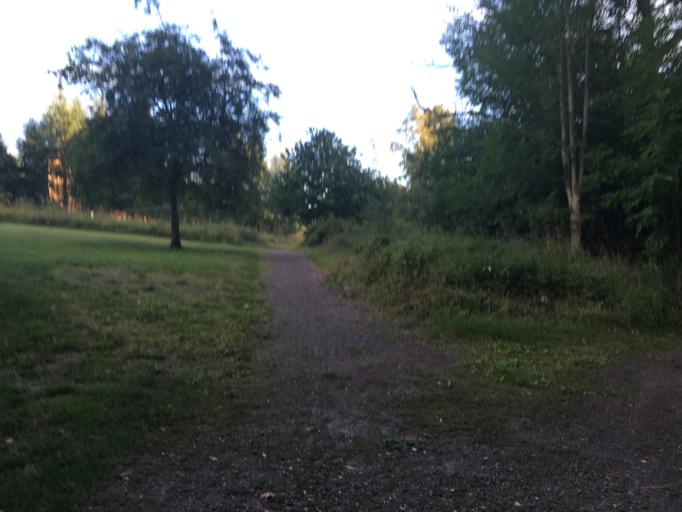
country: SE
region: Kalmar
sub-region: Nybro Kommun
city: Nybro
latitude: 56.9439
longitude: 15.9121
